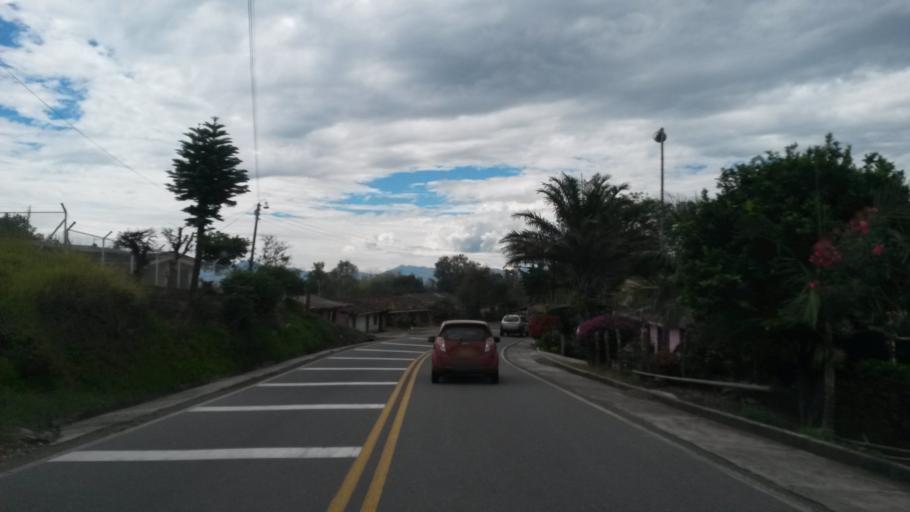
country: CO
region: Cauca
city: Rosas
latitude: 2.3274
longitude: -76.6927
